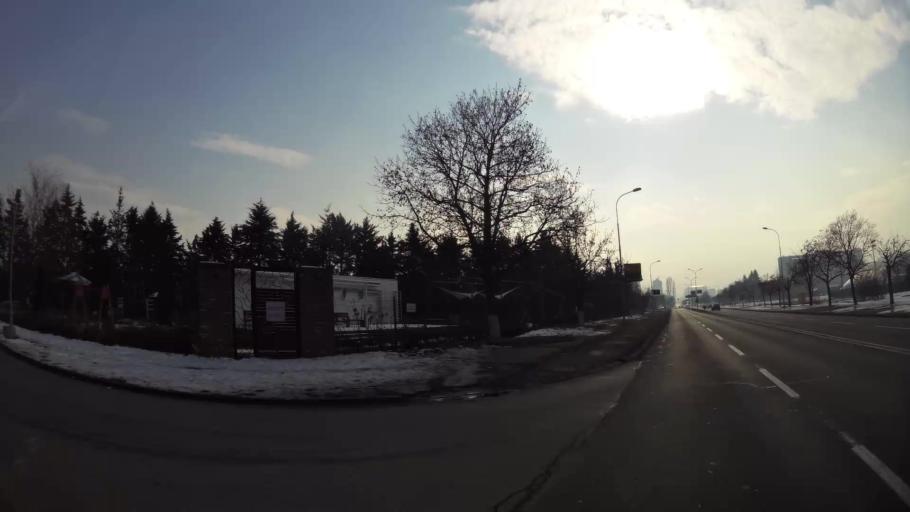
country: MK
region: Karpos
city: Skopje
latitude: 42.0093
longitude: 21.4065
